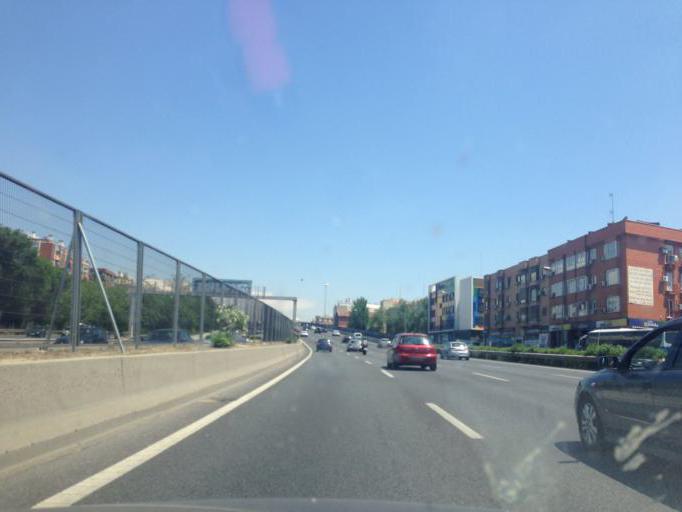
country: ES
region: Madrid
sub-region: Provincia de Madrid
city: Puente de Vallecas
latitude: 40.3954
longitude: -3.6721
